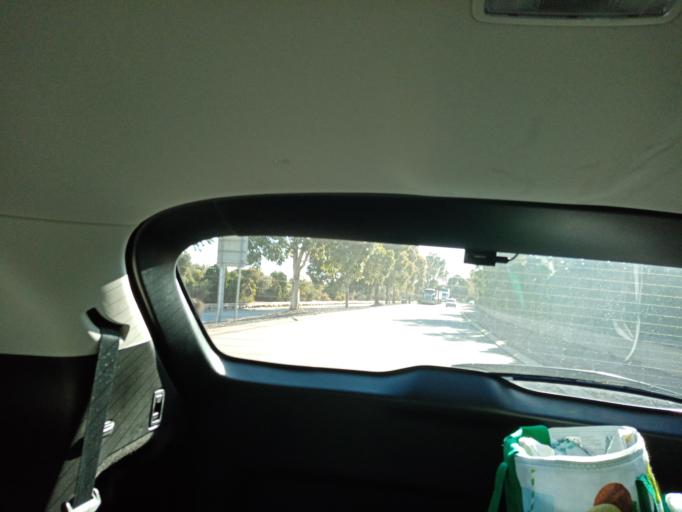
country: AU
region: Western Australia
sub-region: City of Cockburn
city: Yangebup
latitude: -32.1277
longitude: 115.8146
